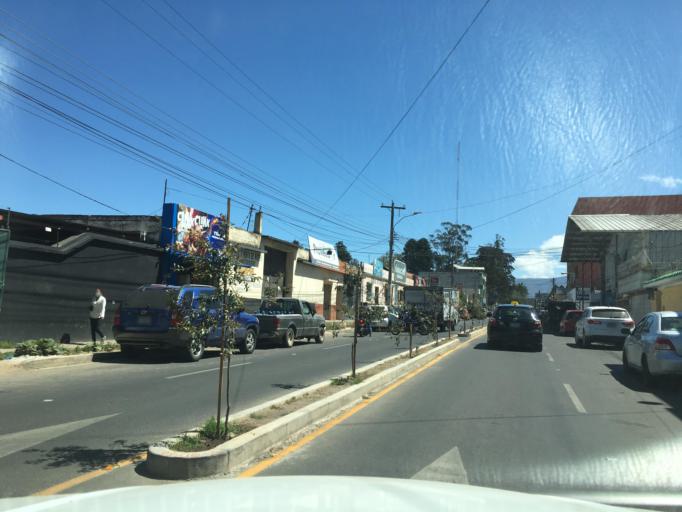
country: GT
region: Quetzaltenango
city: Quetzaltenango
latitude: 14.8450
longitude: -91.5190
